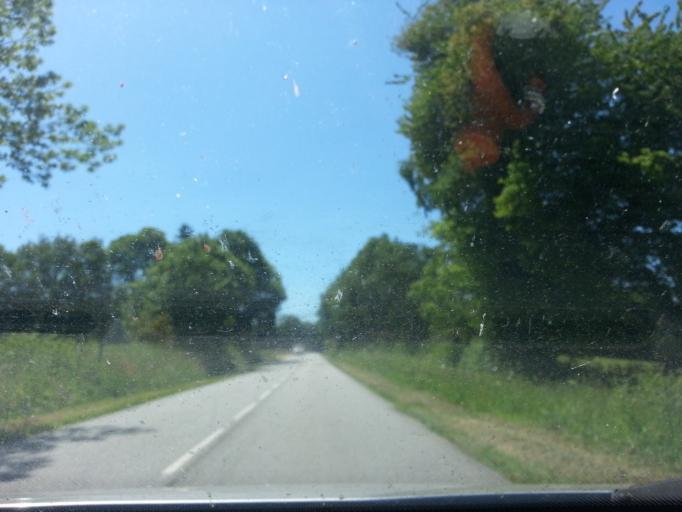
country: FR
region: Brittany
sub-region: Departement du Morbihan
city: Le Faouet
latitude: 48.0567
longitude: -3.4841
